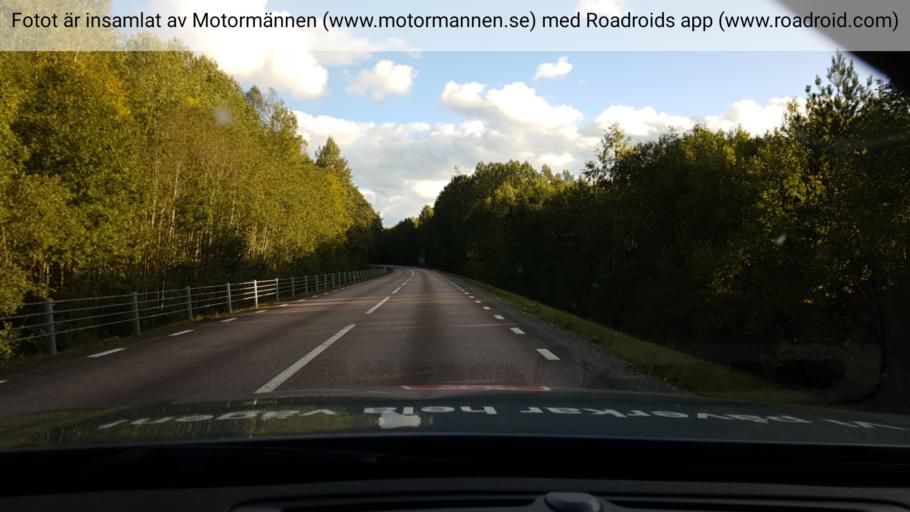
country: SE
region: Vaermland
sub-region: Karlstads Kommun
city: Molkom
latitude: 59.6519
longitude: 13.7110
